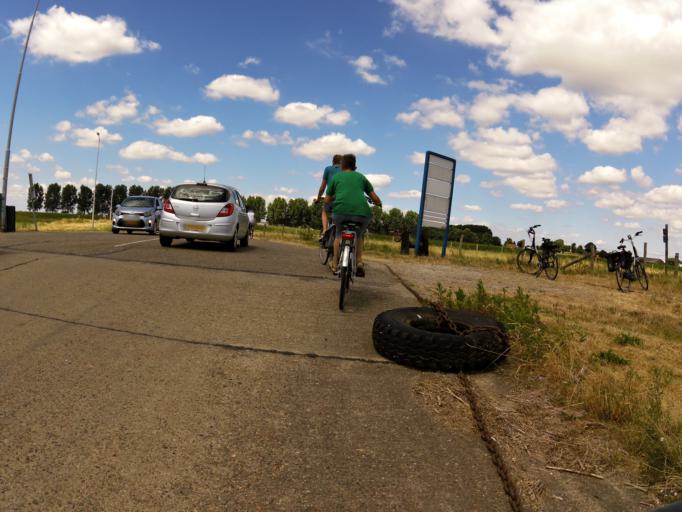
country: NL
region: Gelderland
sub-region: Gemeente Maasdriel
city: Heerewaarden
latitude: 51.7851
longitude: 5.3641
